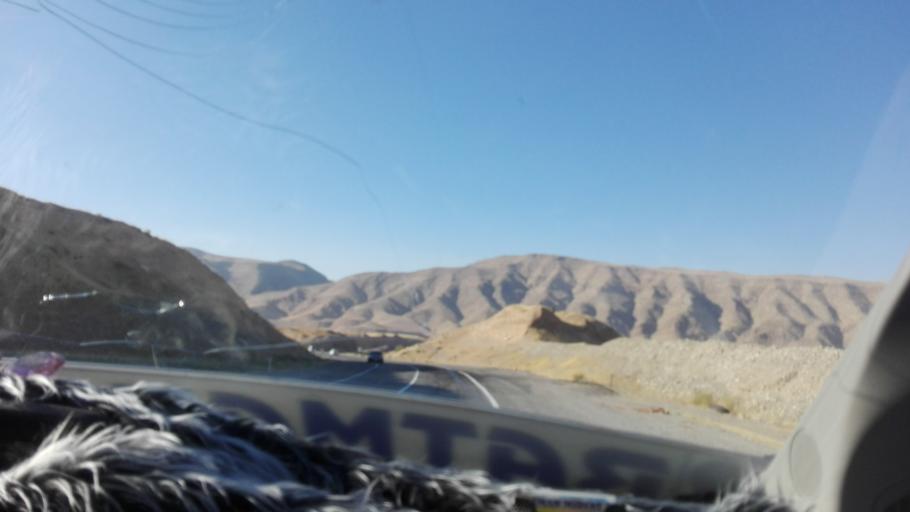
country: TR
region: Batman
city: Hasankeyf
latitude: 37.7114
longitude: 41.4565
